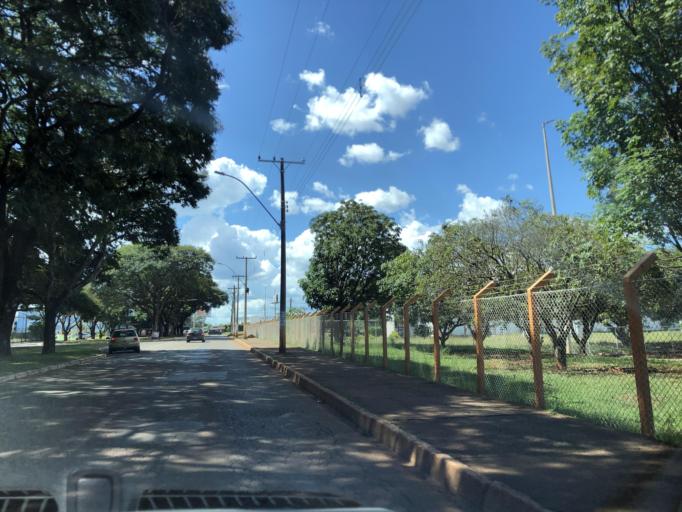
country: BR
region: Federal District
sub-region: Brasilia
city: Brasilia
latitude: -15.8105
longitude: -47.9578
